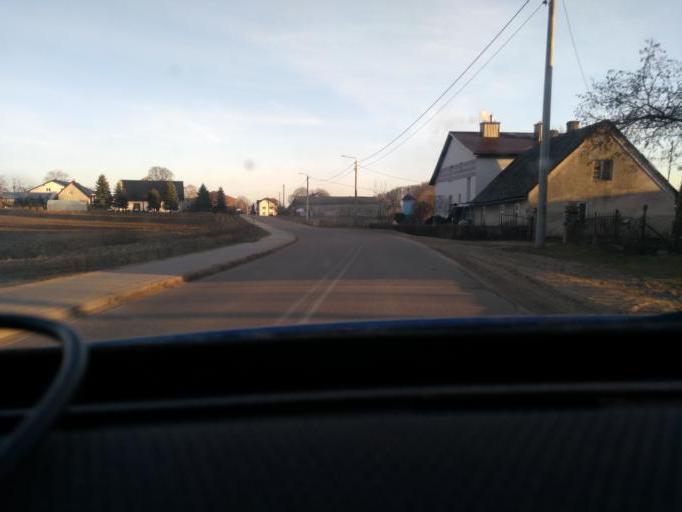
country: PL
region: Pomeranian Voivodeship
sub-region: Powiat kartuski
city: Przodkowo
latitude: 54.4128
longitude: 18.3209
